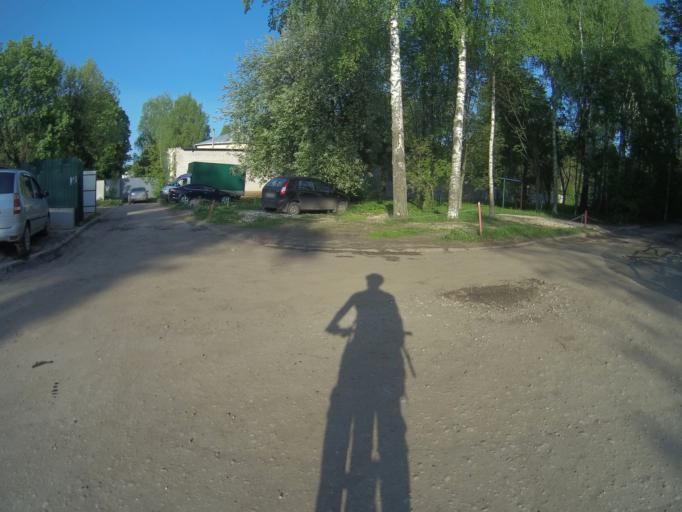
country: RU
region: Vladimir
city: Kommunar
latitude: 56.1684
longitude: 40.4589
